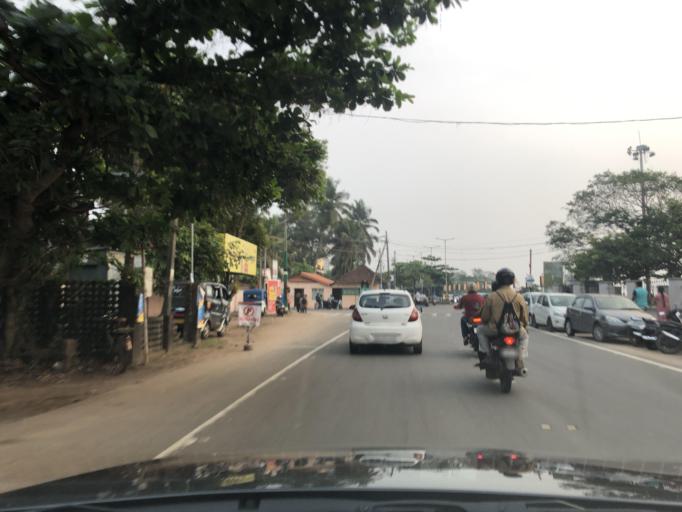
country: IN
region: Kerala
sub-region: Kozhikode
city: Kozhikode
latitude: 11.2587
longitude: 75.7692
